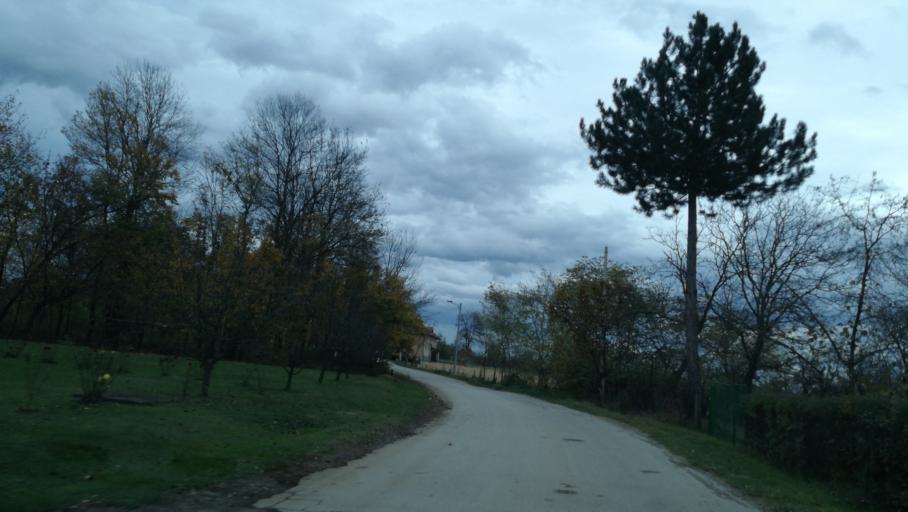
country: RS
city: Prislonica
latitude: 43.9145
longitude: 20.4160
